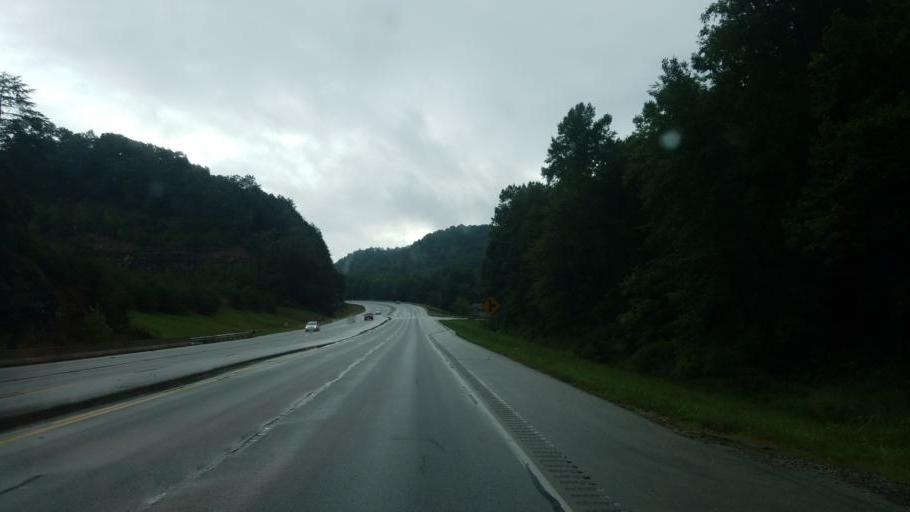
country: US
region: Kentucky
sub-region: Rowan County
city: Morehead
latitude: 38.1798
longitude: -83.4641
